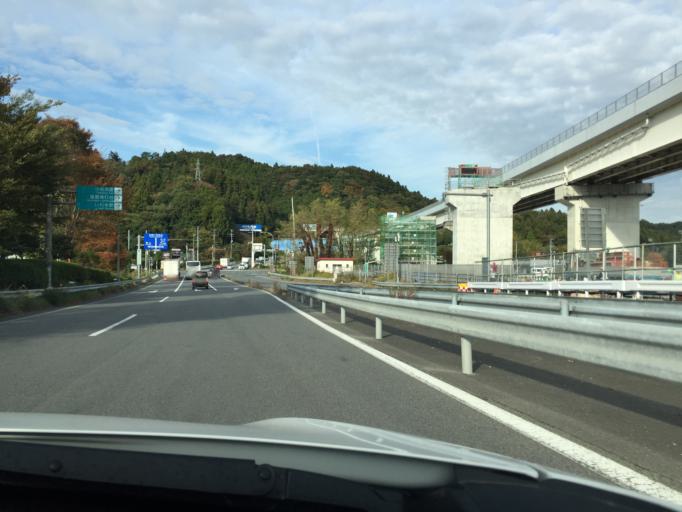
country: JP
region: Fukushima
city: Iwaki
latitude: 37.0692
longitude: 140.8394
